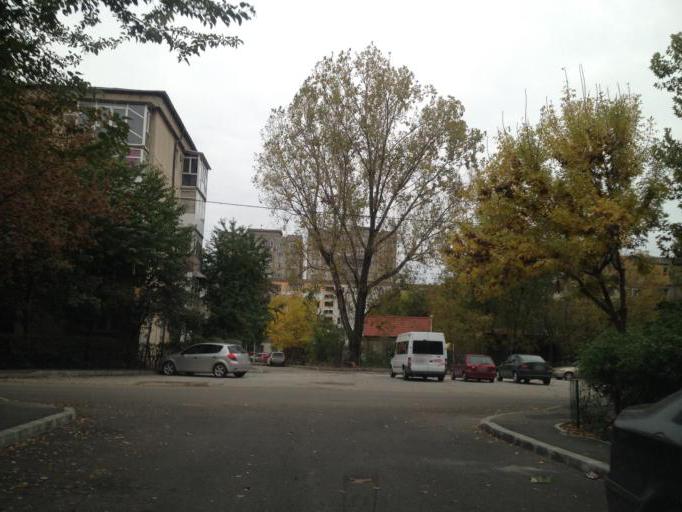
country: RO
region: Dolj
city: Craiova
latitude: 44.3362
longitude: 23.7875
